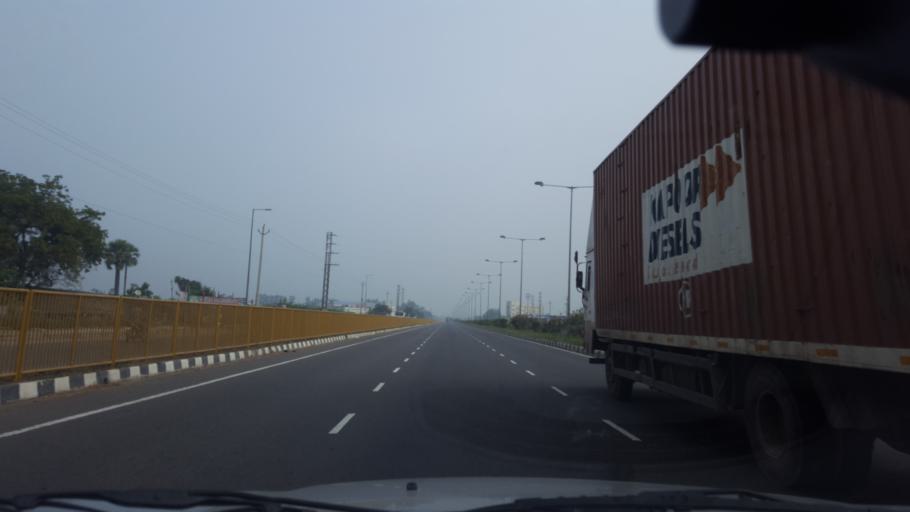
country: IN
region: Andhra Pradesh
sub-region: Guntur
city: Chilakalurupet
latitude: 15.9954
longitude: 80.1086
